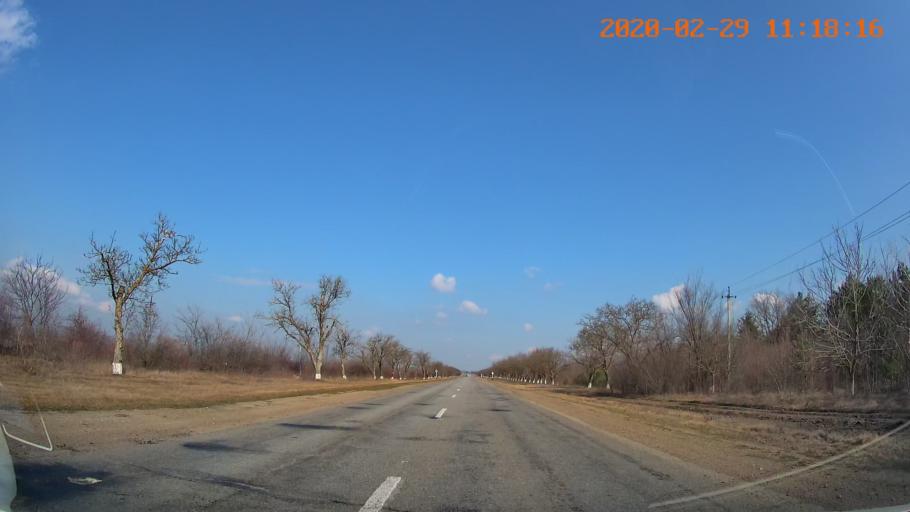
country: MD
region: Telenesti
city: Cocieri
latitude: 47.3325
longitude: 29.1724
